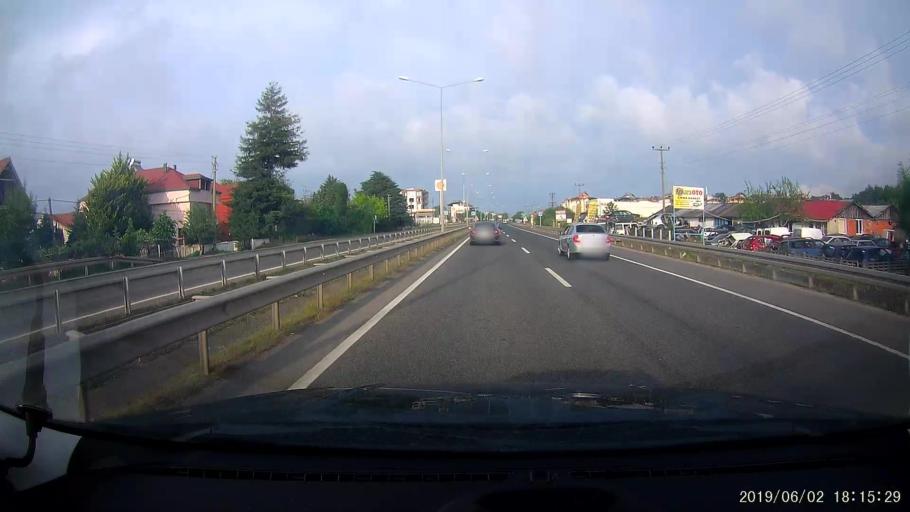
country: TR
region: Ordu
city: Unieh
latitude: 41.1059
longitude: 37.3788
